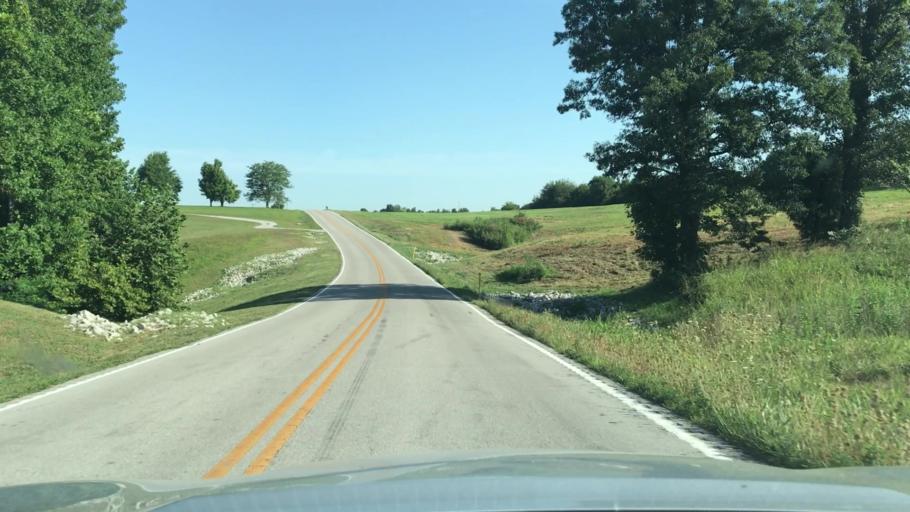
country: US
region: Kentucky
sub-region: Muhlenberg County
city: Greenville
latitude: 37.0139
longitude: -87.1308
